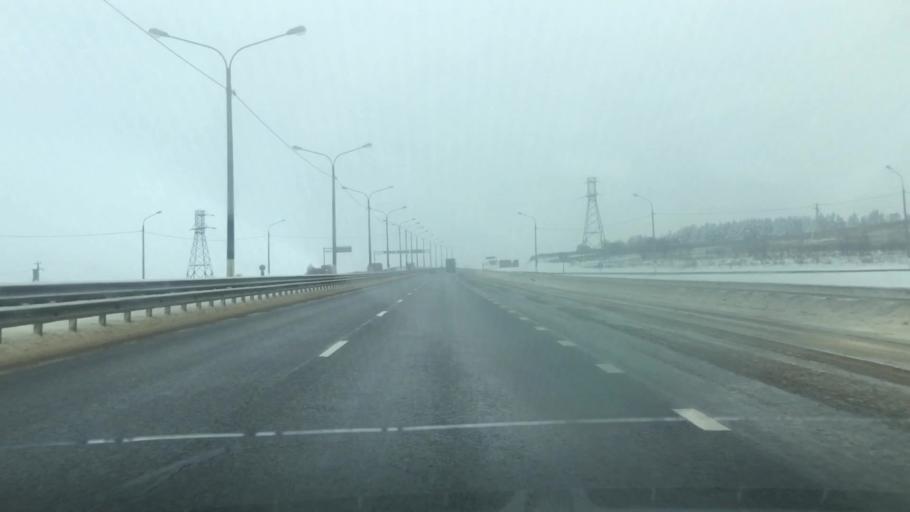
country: RU
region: Tula
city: Yefremov
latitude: 53.1616
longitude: 38.2489
